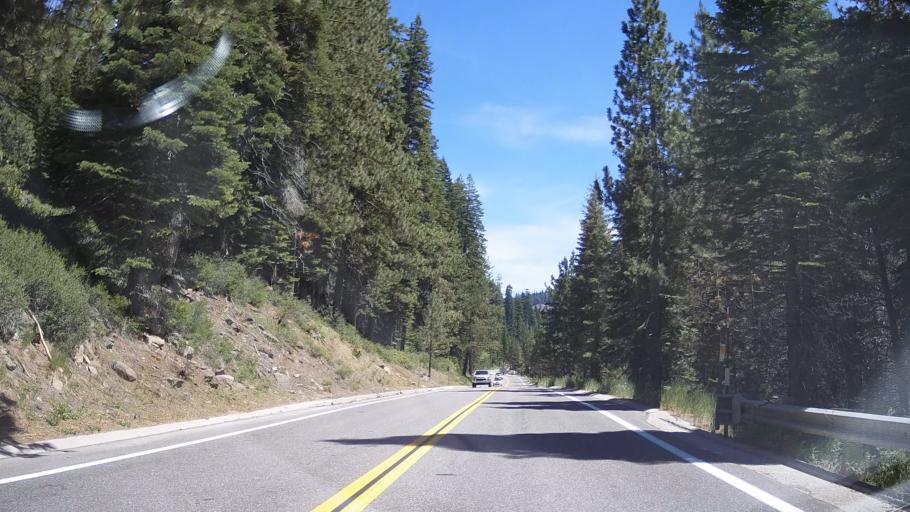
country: US
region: California
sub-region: Placer County
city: Sunnyside-Tahoe City
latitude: 39.1806
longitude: -120.1936
